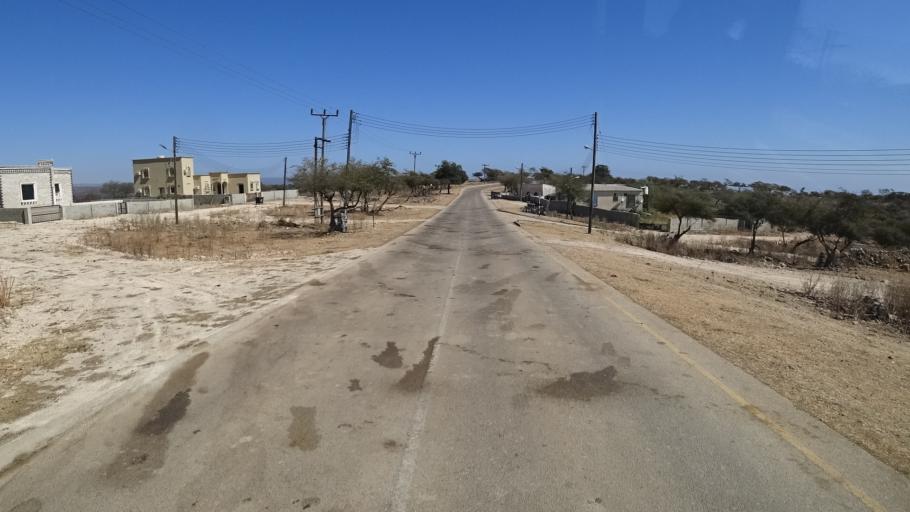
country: YE
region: Al Mahrah
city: Hawf
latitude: 16.7789
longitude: 53.3345
